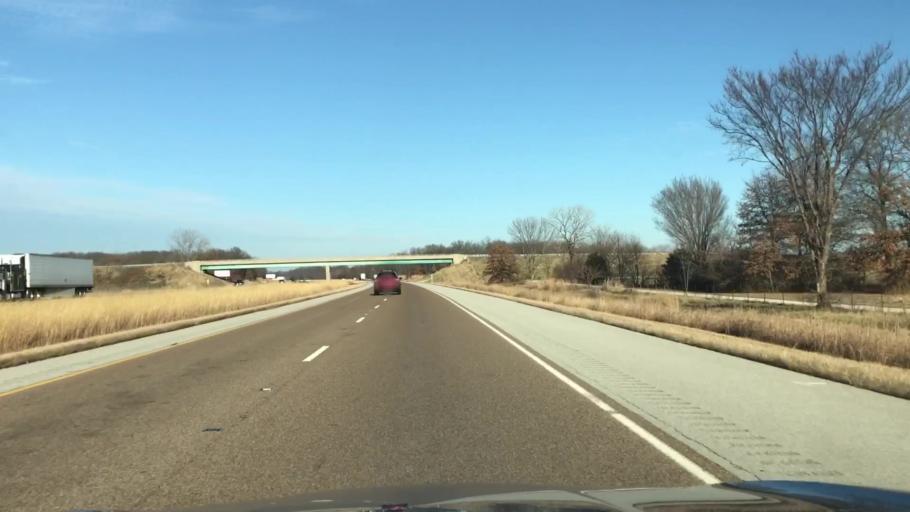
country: US
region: Illinois
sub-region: Macoupin County
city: Mount Olive
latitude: 39.0916
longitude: -89.7425
